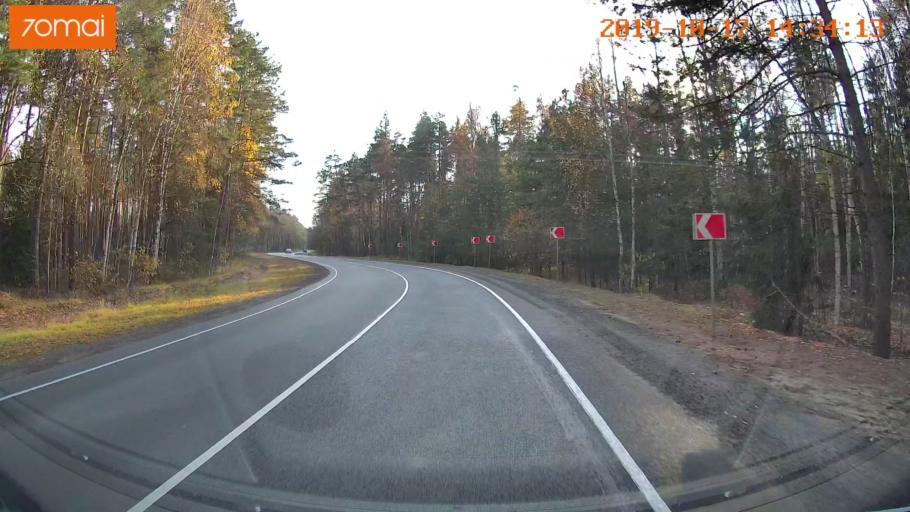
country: RU
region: Rjazan
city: Solotcha
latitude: 54.9152
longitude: 39.9976
